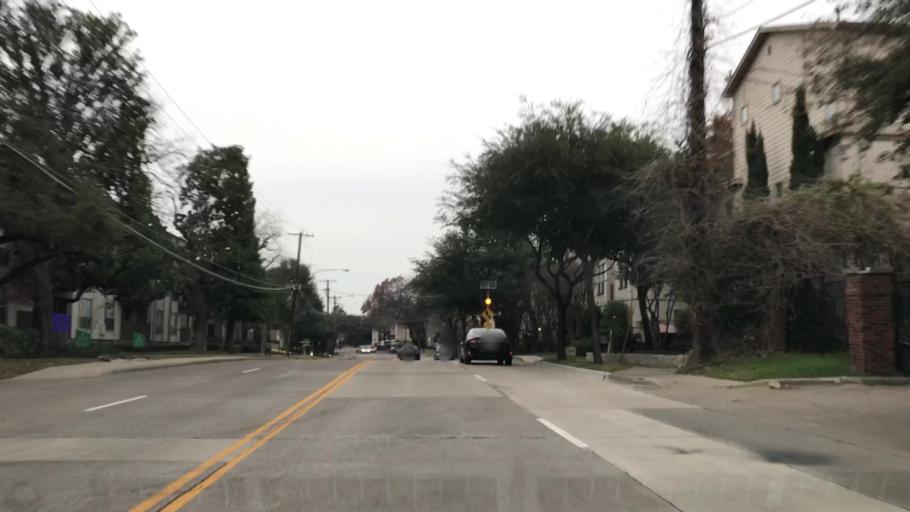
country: US
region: Texas
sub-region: Dallas County
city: Highland Park
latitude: 32.8195
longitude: -96.8213
